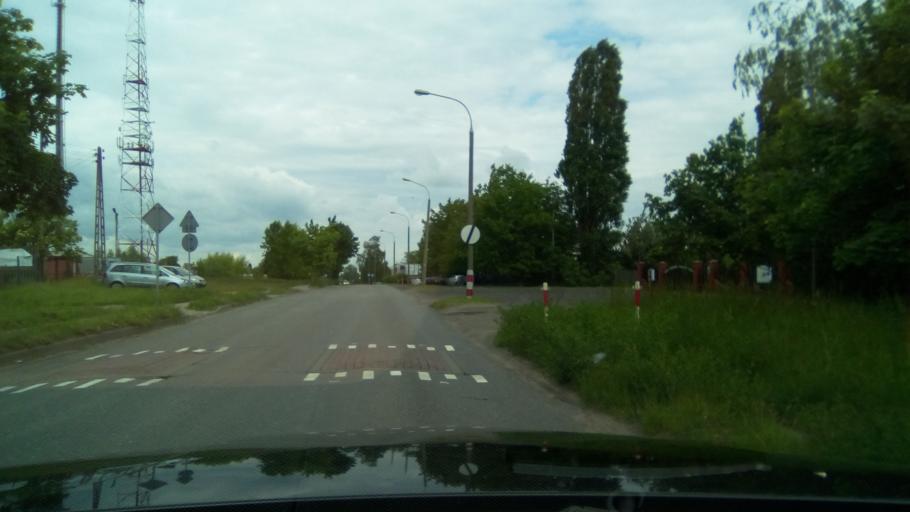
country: PL
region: Greater Poland Voivodeship
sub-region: Powiat gnieznienski
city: Gniezno
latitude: 52.5230
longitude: 17.6116
